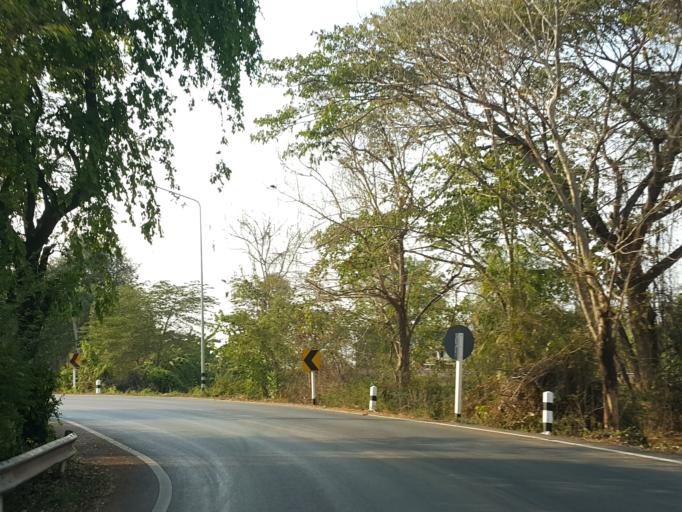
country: TH
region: Uttaradit
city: Phichai
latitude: 17.1695
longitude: 100.1085
